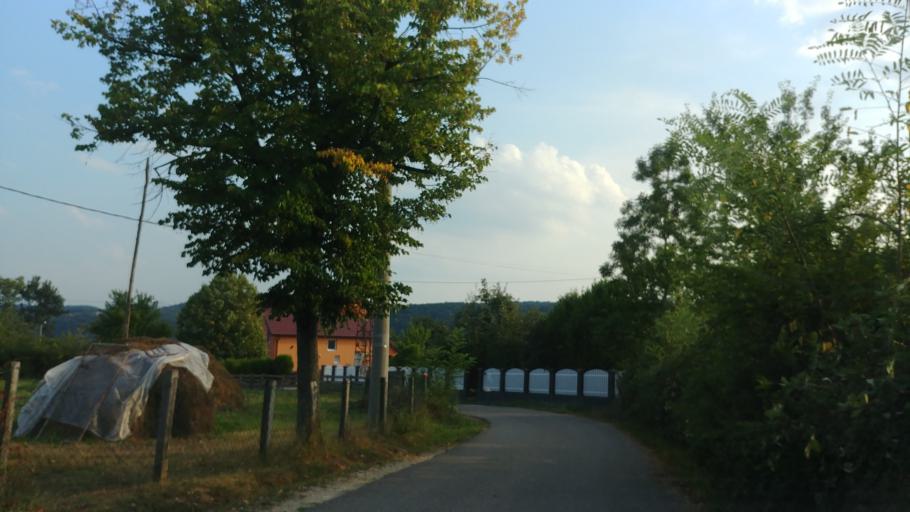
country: BA
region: Republika Srpska
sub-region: Opstina Ugljevik
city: Ugljevik
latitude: 44.7029
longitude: 19.0098
